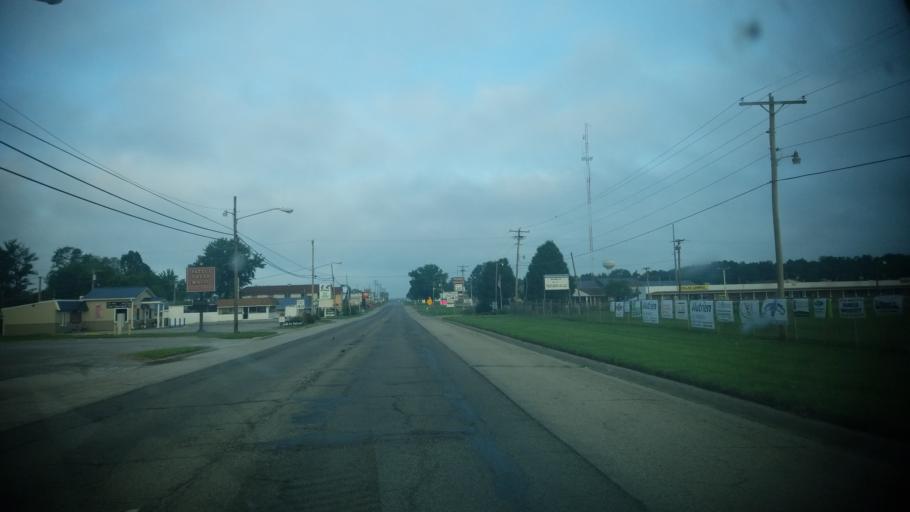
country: US
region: Illinois
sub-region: Wayne County
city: Fairfield
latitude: 38.3797
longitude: -88.3791
